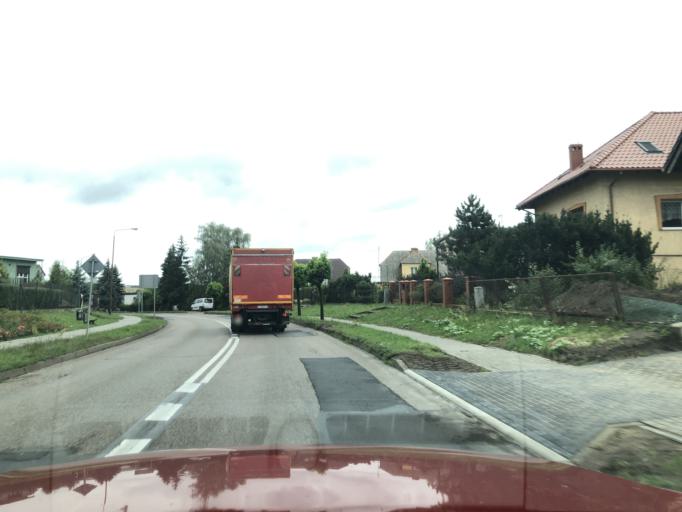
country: PL
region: Greater Poland Voivodeship
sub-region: Powiat szamotulski
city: Wronki
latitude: 52.7029
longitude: 16.3868
